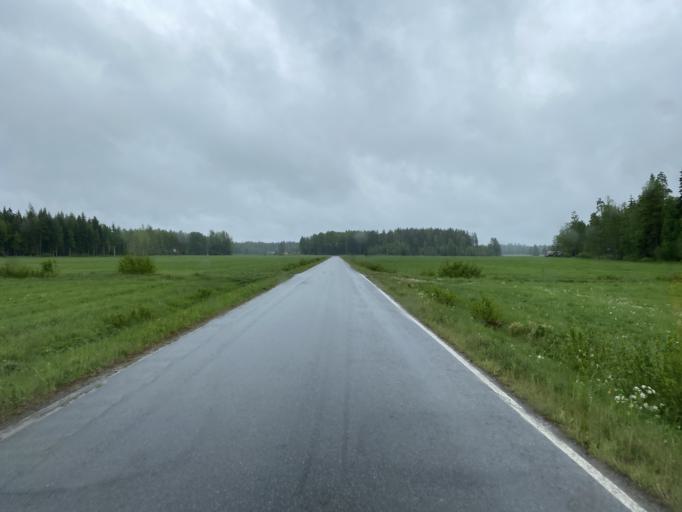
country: FI
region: Haeme
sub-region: Forssa
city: Humppila
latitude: 61.0518
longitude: 23.3455
